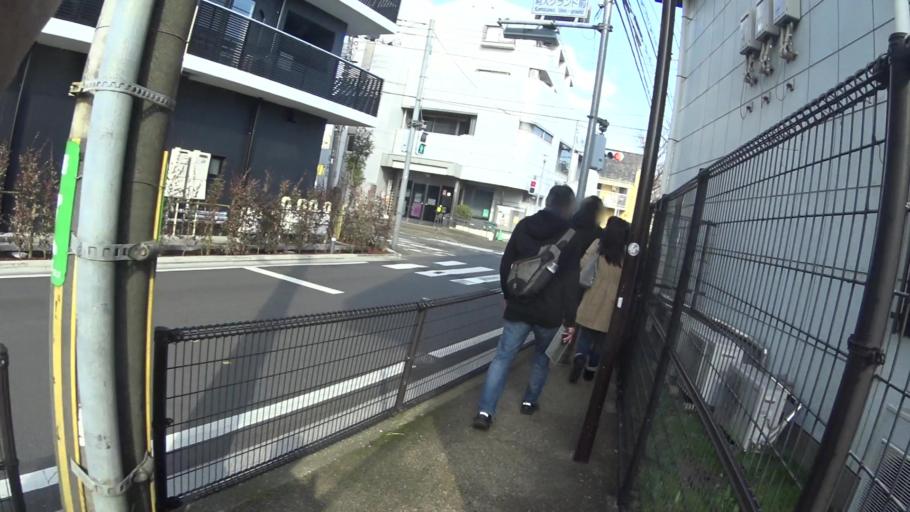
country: JP
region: Tokyo
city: Mitaka-shi
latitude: 35.6571
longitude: 139.5995
